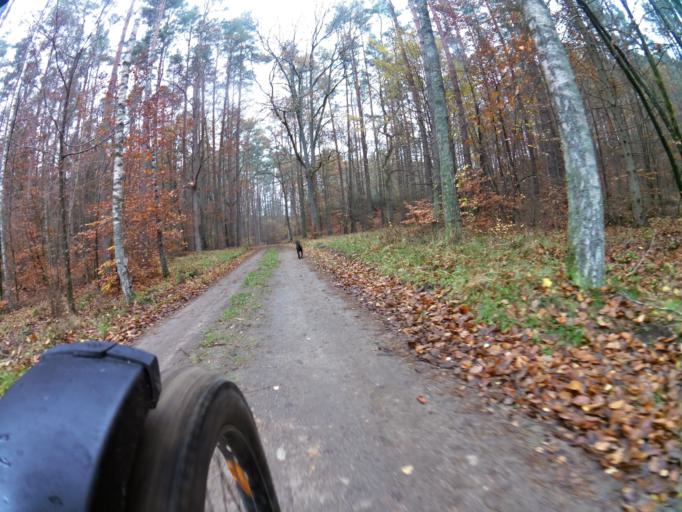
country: PL
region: Pomeranian Voivodeship
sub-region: Powiat wejherowski
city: Orle
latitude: 54.6945
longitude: 18.1561
